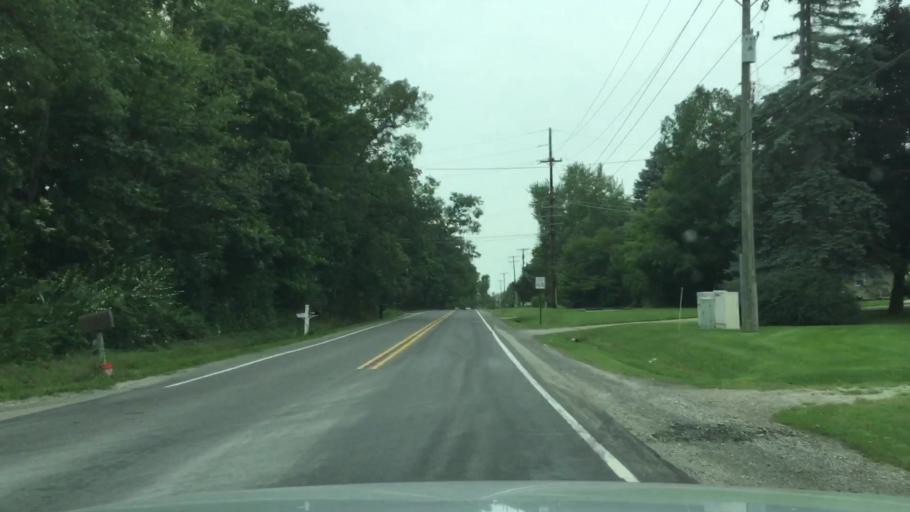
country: US
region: Michigan
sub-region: Washtenaw County
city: Ypsilanti
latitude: 42.2013
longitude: -83.6701
